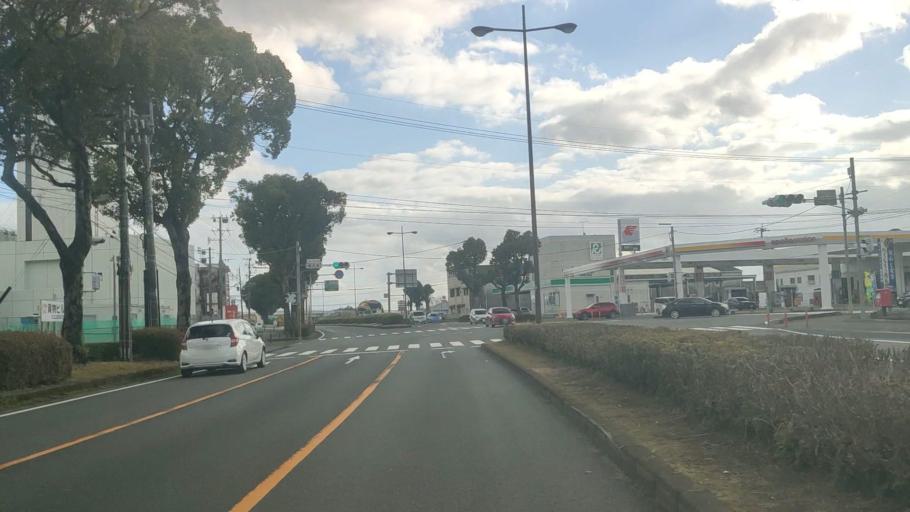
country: JP
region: Kagoshima
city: Kokubu-matsuki
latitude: 31.7954
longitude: 130.7182
